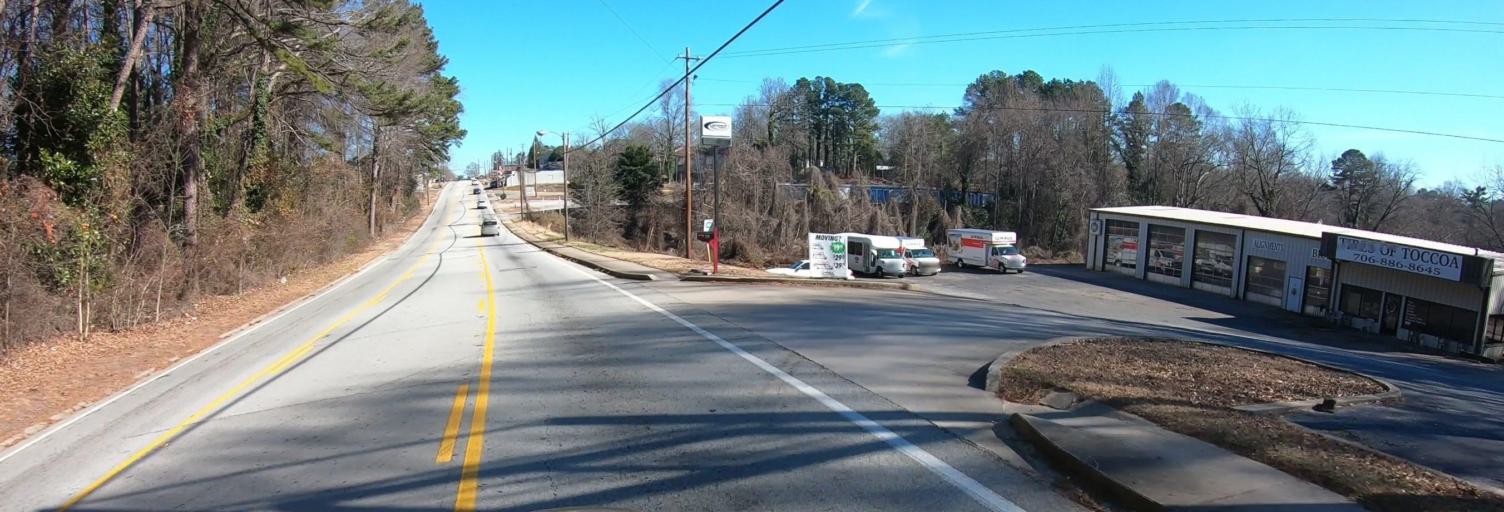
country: US
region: Georgia
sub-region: Stephens County
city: Toccoa
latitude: 34.5762
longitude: -83.3192
